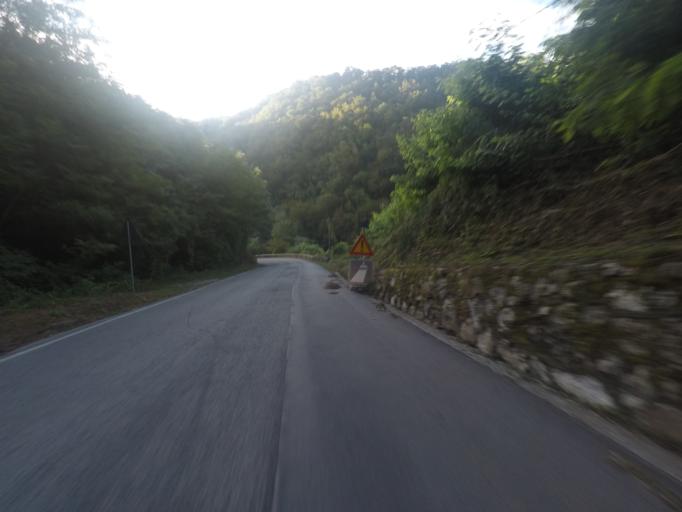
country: IT
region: Tuscany
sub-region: Provincia di Lucca
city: Valdottavo
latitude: 43.9631
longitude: 10.4641
